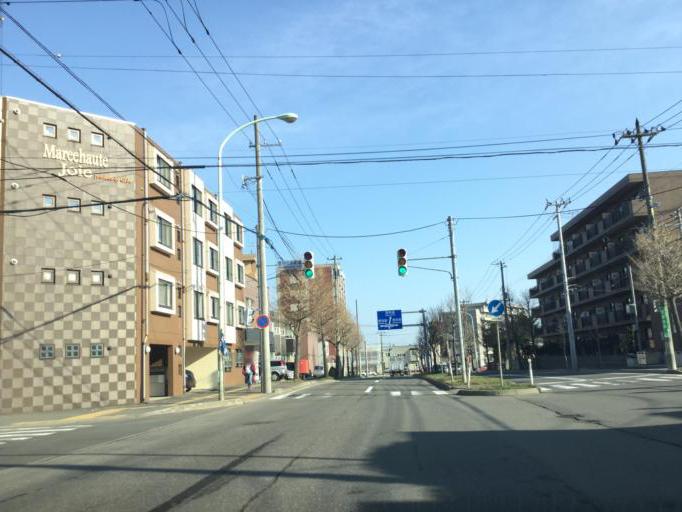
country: JP
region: Hokkaido
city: Ebetsu
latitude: 43.0428
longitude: 141.4686
